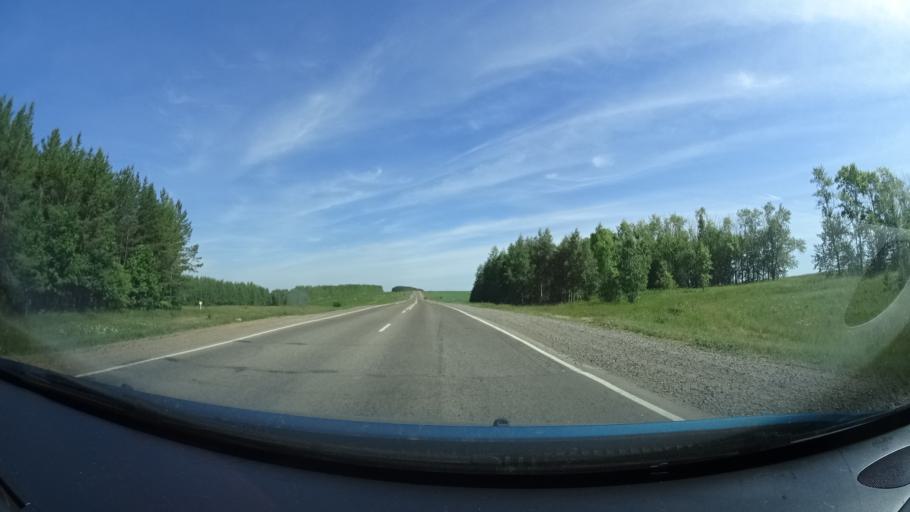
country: RU
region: Bashkortostan
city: Blagoveshchensk
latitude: 55.1415
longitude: 55.8483
